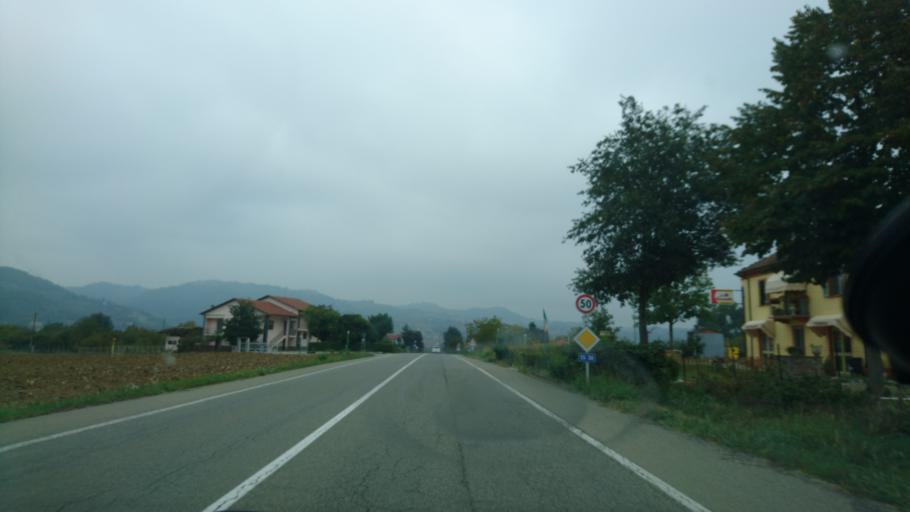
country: IT
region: Piedmont
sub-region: Provincia di Alessandria
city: Bistagno
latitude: 44.6512
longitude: 8.3620
